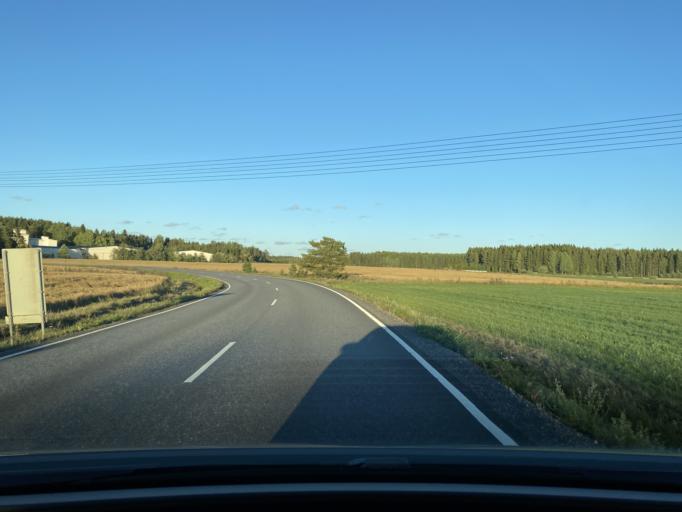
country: FI
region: Varsinais-Suomi
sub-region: Loimaa
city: Alastaro
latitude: 60.9551
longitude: 22.8740
